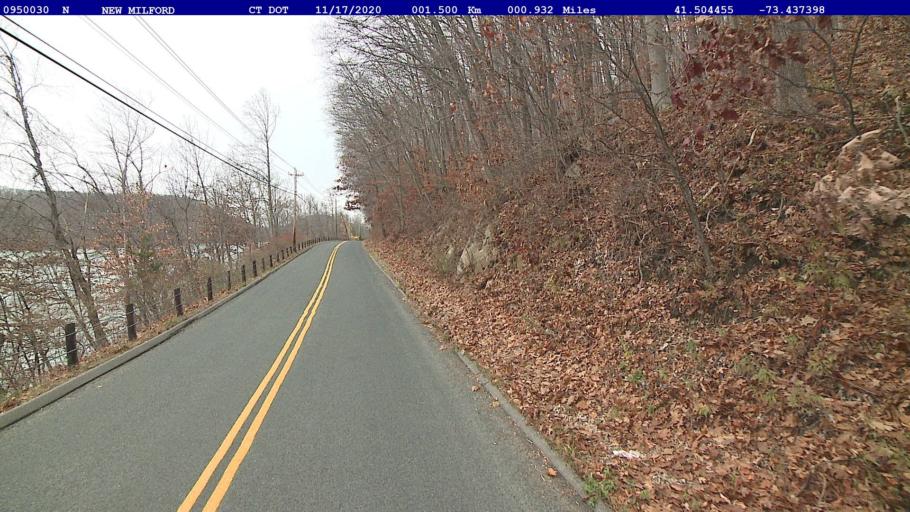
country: US
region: Connecticut
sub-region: Litchfield County
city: New Milford
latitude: 41.5045
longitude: -73.4374
